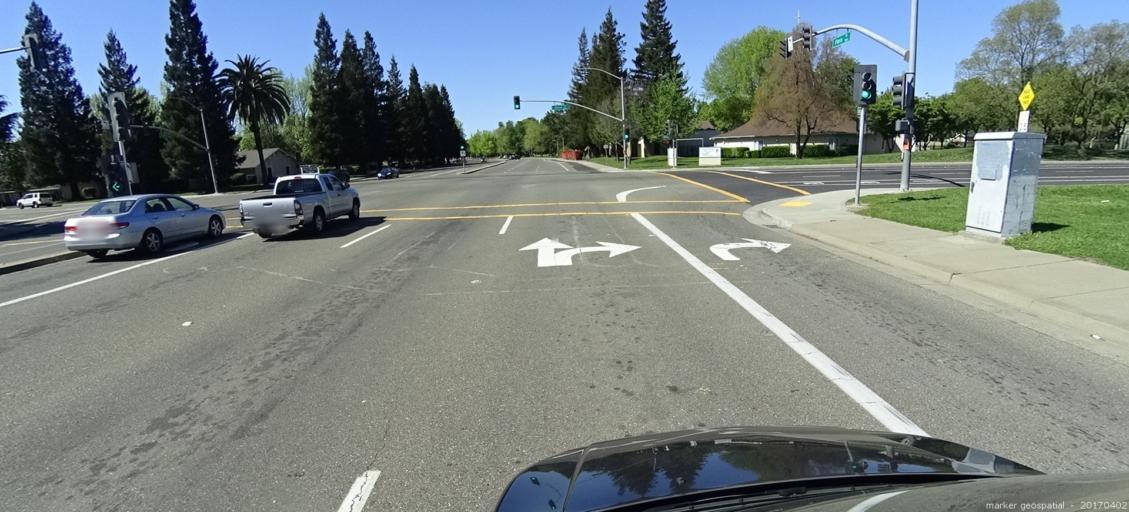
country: US
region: California
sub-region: Yolo County
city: West Sacramento
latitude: 38.5040
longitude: -121.5376
